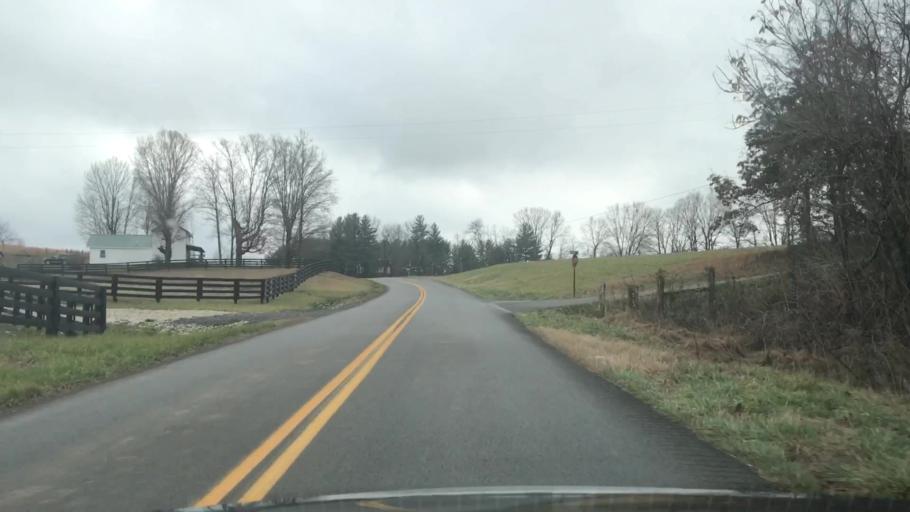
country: US
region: Kentucky
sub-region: Monroe County
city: Tompkinsville
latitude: 36.7244
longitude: -85.7097
